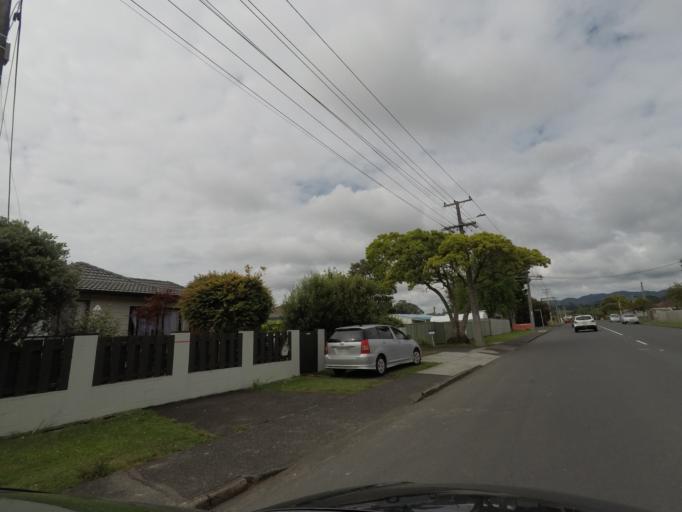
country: NZ
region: Auckland
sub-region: Auckland
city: Waitakere
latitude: -36.8984
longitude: 174.6246
